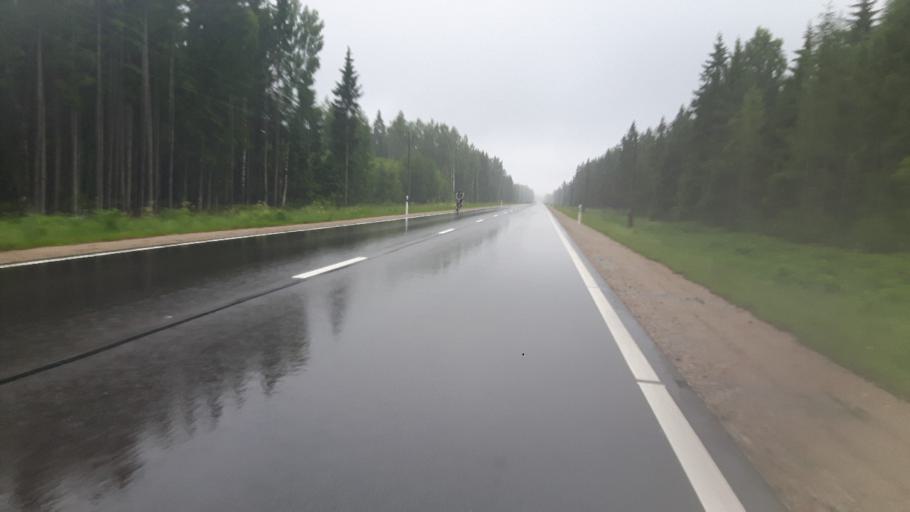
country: LV
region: Rucavas
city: Rucava
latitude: 56.1692
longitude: 21.1442
